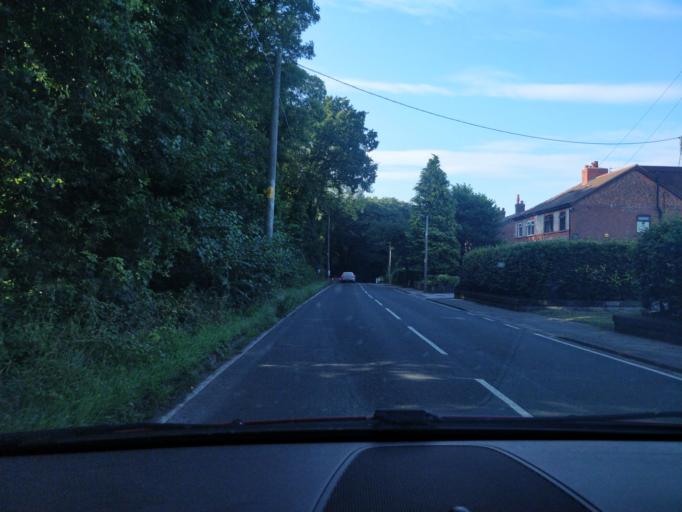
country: GB
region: England
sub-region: Lancashire
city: Banks
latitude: 53.6544
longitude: -2.8782
